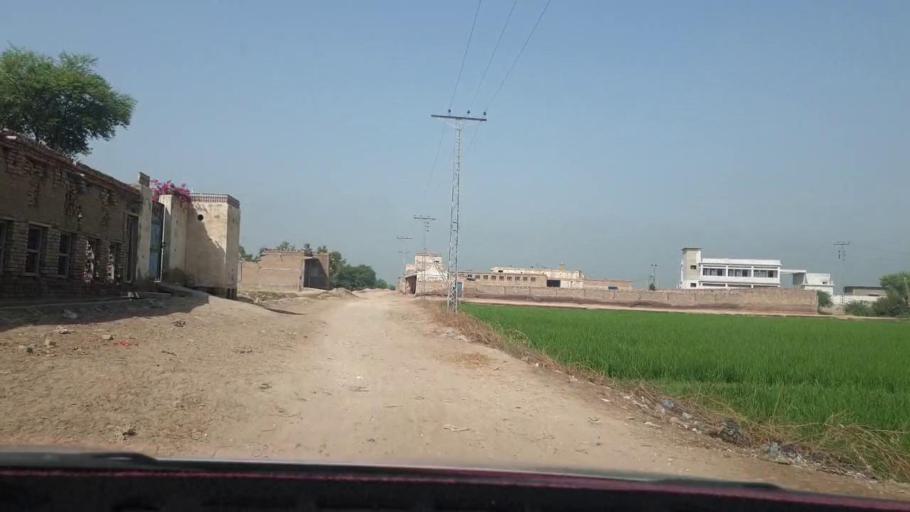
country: PK
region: Sindh
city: Nasirabad
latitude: 27.4242
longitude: 67.9076
